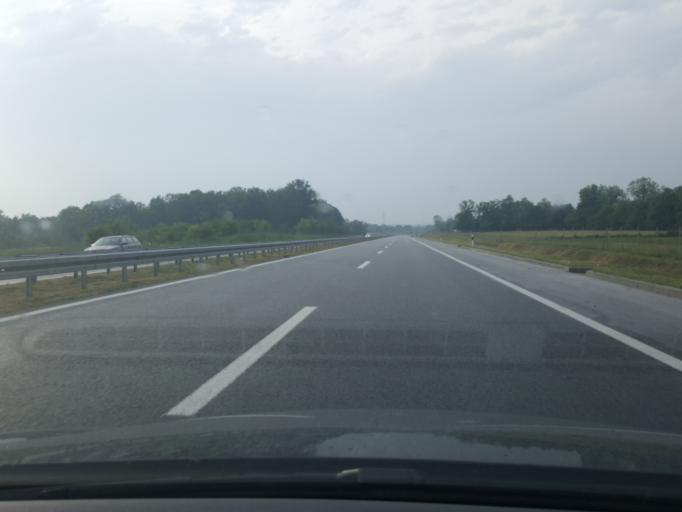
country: RS
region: Central Serbia
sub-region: Kolubarski Okrug
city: Lajkovac
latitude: 44.3898
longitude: 20.1045
